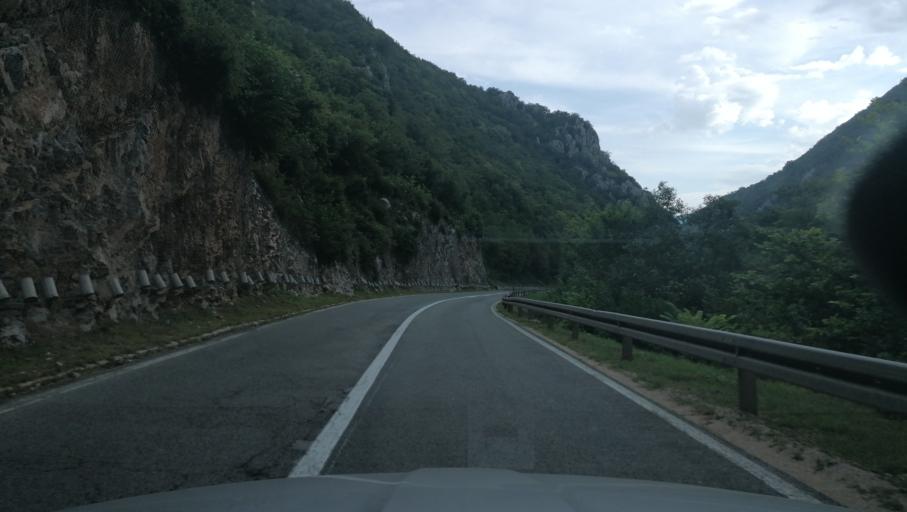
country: BA
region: Republika Srpska
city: Hiseti
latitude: 44.6009
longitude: 17.1318
